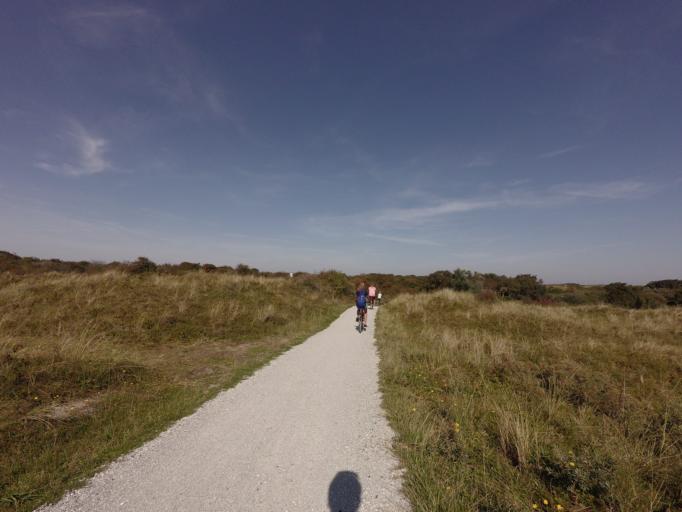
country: NL
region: Friesland
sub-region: Gemeente Schiermonnikoog
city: Schiermonnikoog
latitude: 53.4762
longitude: 6.1387
